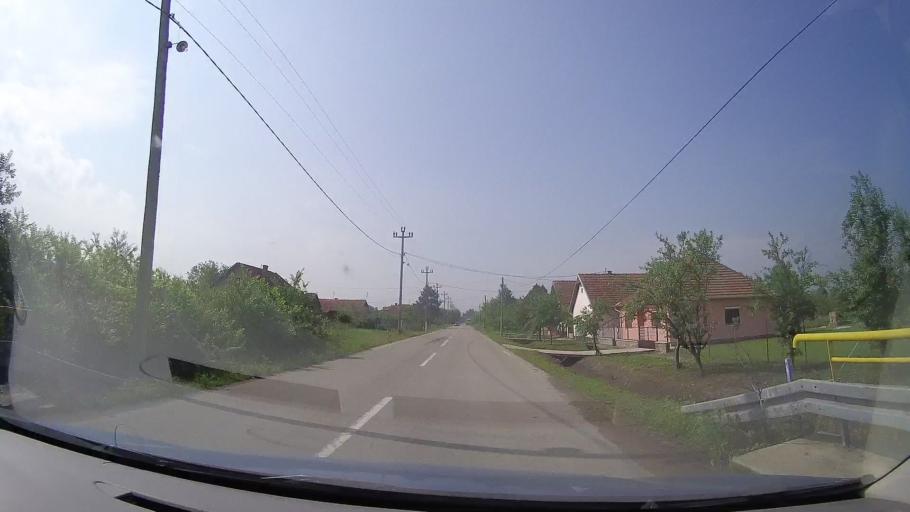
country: RS
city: Jasa Tomic
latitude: 45.4545
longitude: 20.8555
